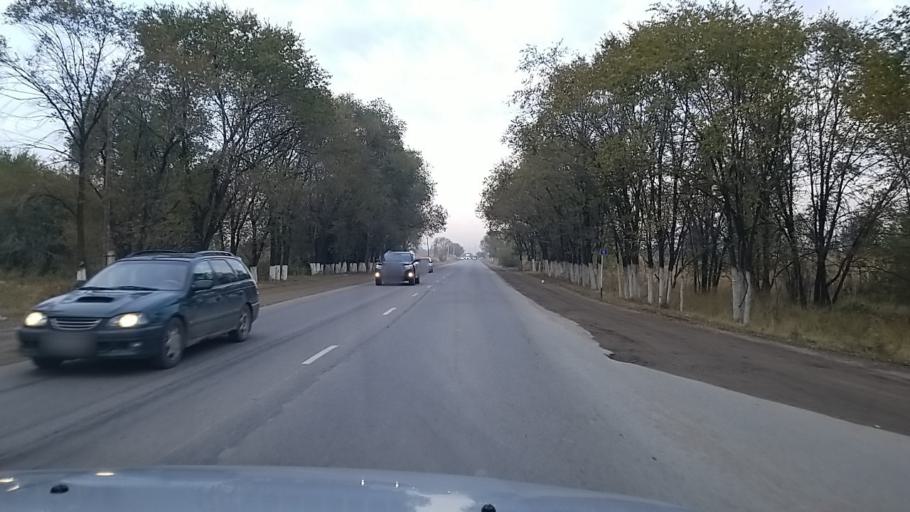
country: KZ
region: Almaty Oblysy
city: Burunday
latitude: 43.3565
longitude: 76.7925
